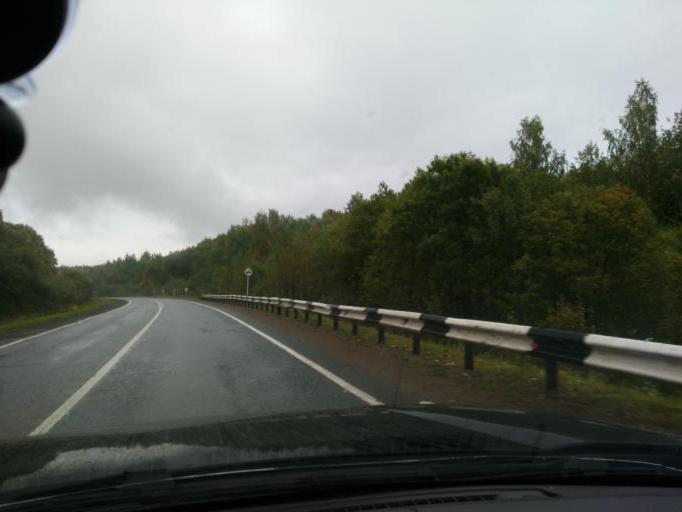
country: RU
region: Perm
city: Yugo-Kamskiy
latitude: 57.7325
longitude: 55.7048
